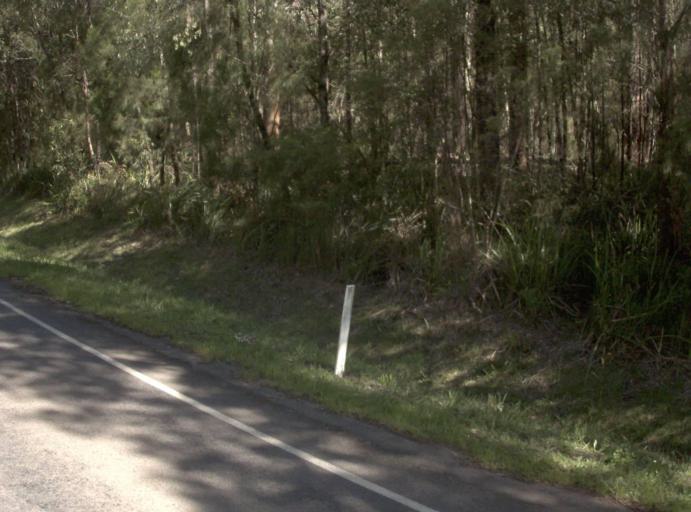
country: AU
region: Victoria
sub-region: Yarra Ranges
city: Millgrove
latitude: -37.8809
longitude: 145.8559
